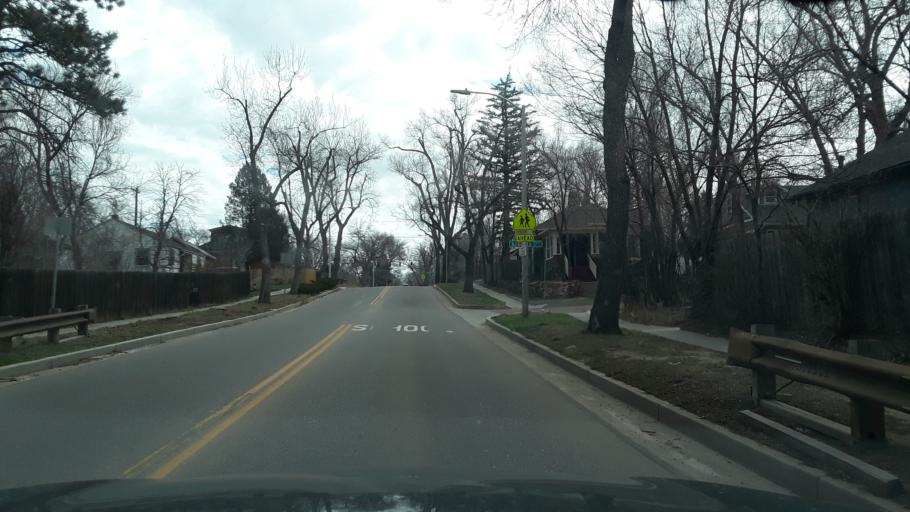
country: US
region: Colorado
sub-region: El Paso County
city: Colorado Springs
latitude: 38.8502
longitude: -104.8089
